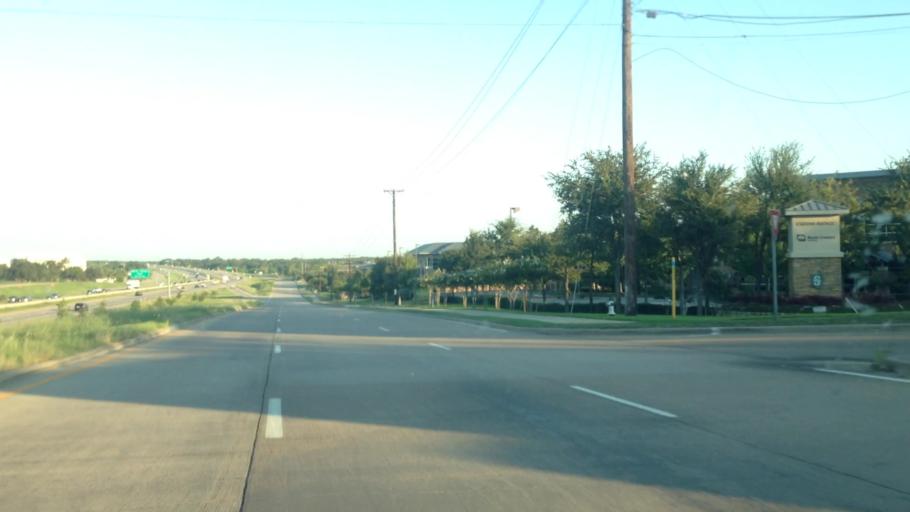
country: US
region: Texas
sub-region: Tarrant County
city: Southlake
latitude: 32.9527
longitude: -97.1344
